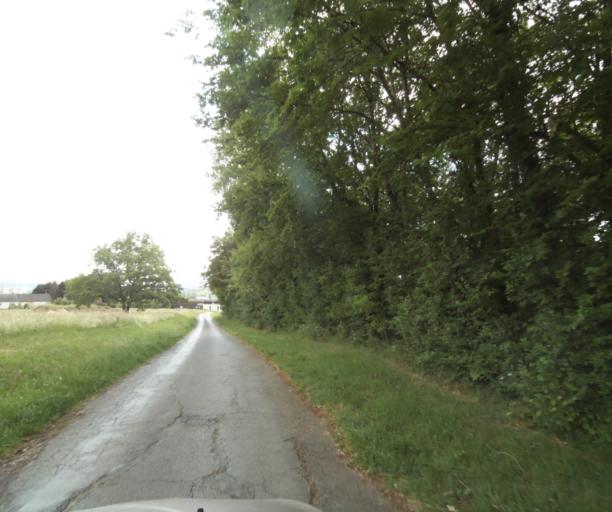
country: FR
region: Champagne-Ardenne
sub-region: Departement des Ardennes
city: Montcy-Notre-Dame
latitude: 49.7634
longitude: 4.7327
